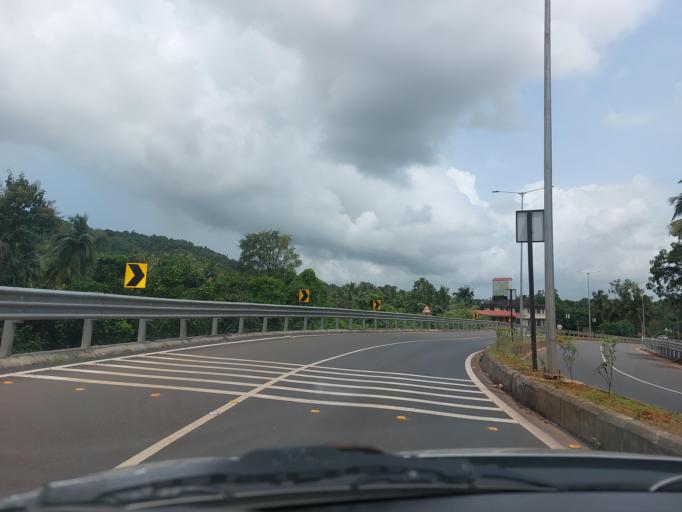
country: IN
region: Goa
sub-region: North Goa
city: Queula
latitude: 15.3851
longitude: 74.0004
